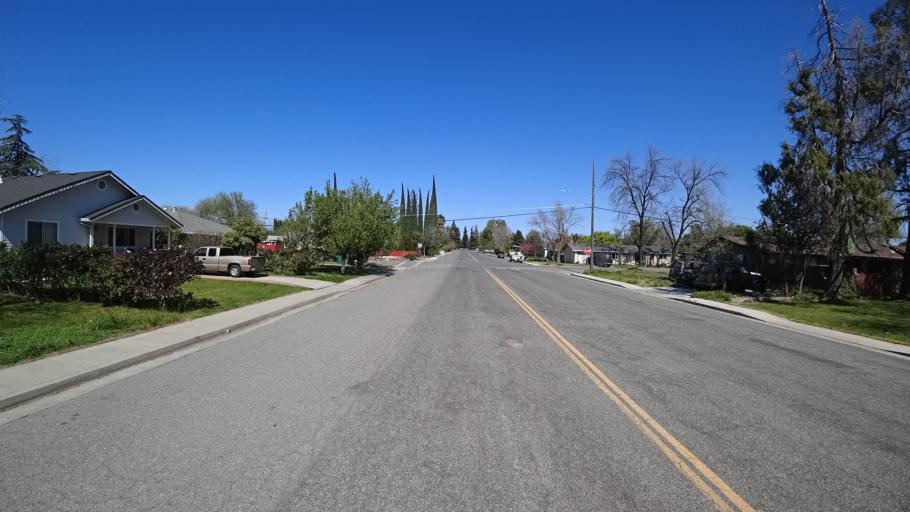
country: US
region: California
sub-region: Glenn County
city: Hamilton City
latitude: 39.7415
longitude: -122.0165
